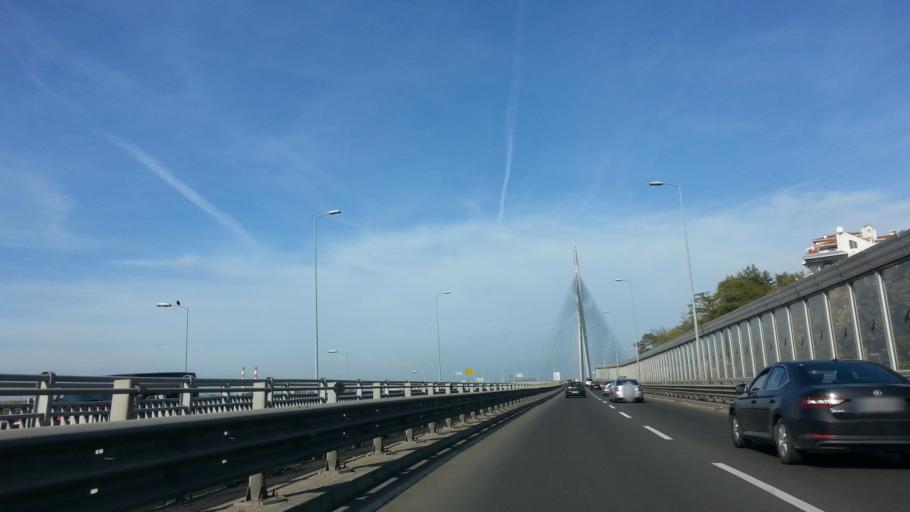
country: RS
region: Central Serbia
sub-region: Belgrade
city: Cukarica
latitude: 44.7870
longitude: 20.4313
